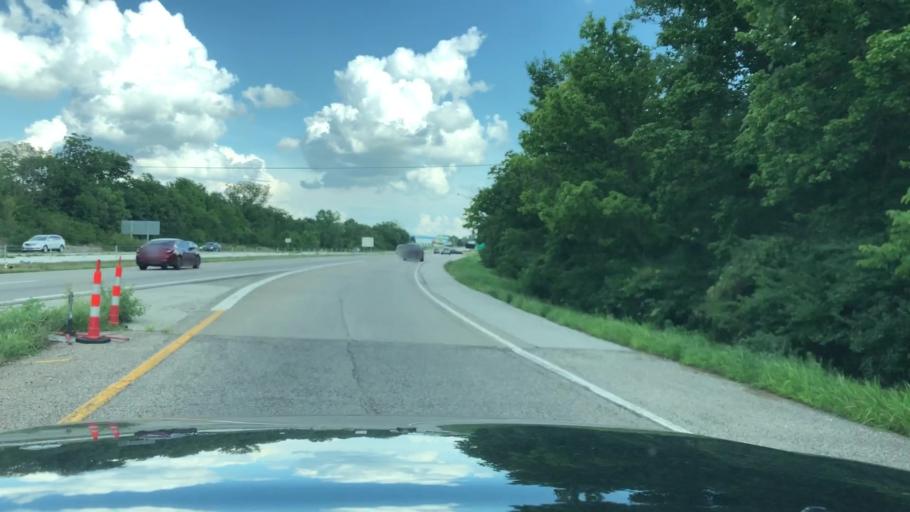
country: US
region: Missouri
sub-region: Saint Charles County
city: Wentzville
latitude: 38.8211
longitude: -90.8477
